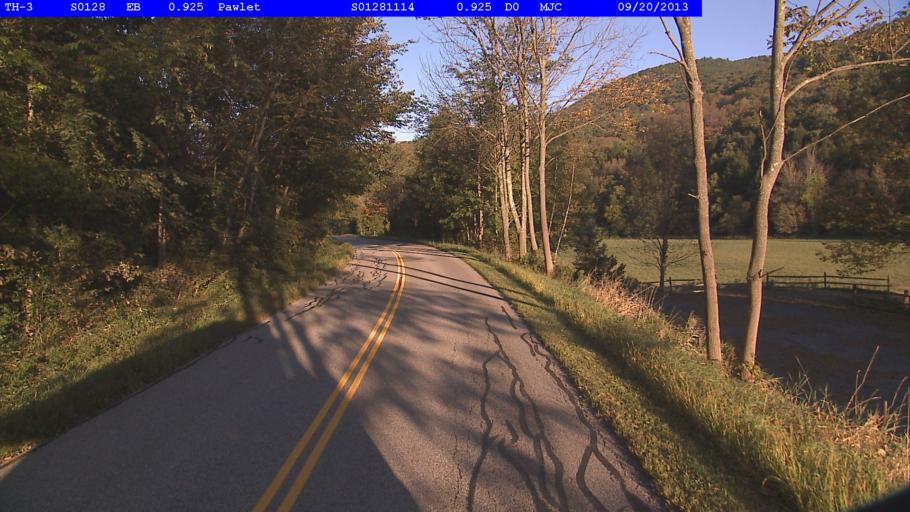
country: US
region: New York
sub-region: Washington County
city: Granville
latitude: 43.3707
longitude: -73.2124
